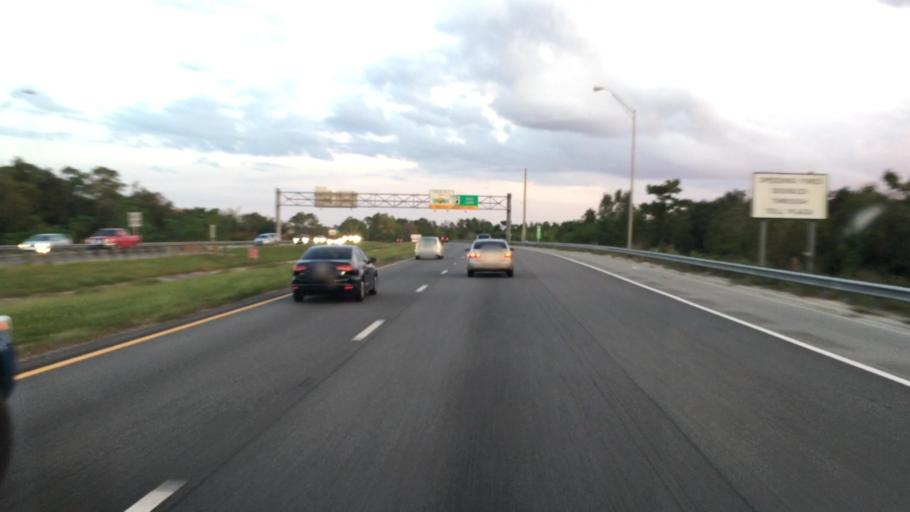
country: US
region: Florida
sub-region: Seminole County
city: Sanford
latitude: 28.7514
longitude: -81.2666
